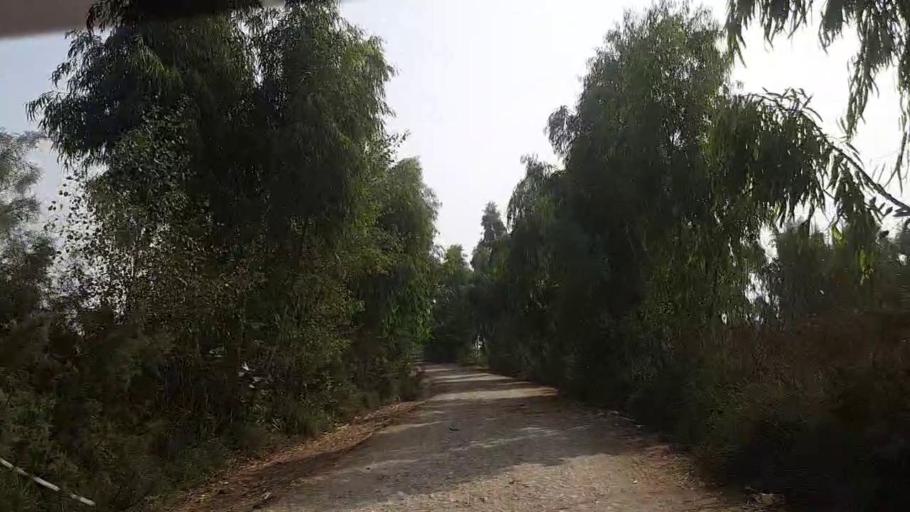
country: PK
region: Sindh
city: Madeji
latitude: 27.7340
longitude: 68.4358
